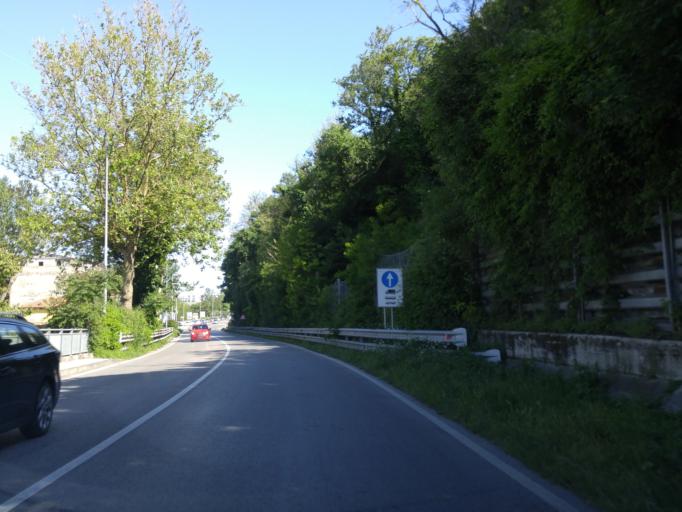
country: IT
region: The Marches
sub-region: Provincia di Pesaro e Urbino
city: Pesaro
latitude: 43.9063
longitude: 12.9239
